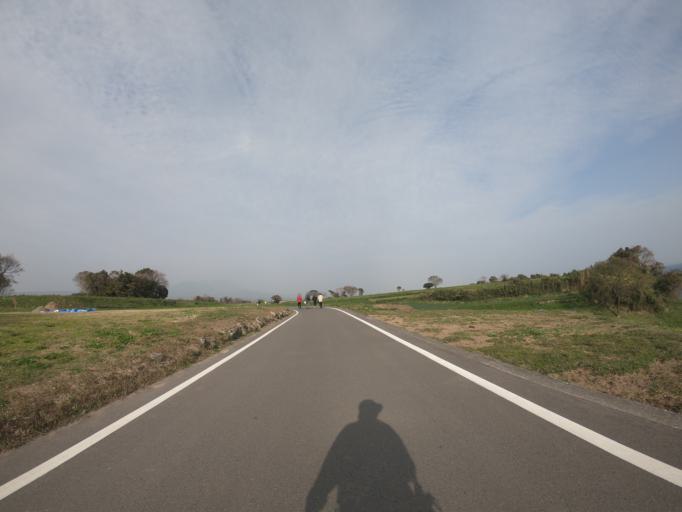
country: JP
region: Kumamoto
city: Hondo
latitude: 32.6306
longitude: 130.2545
